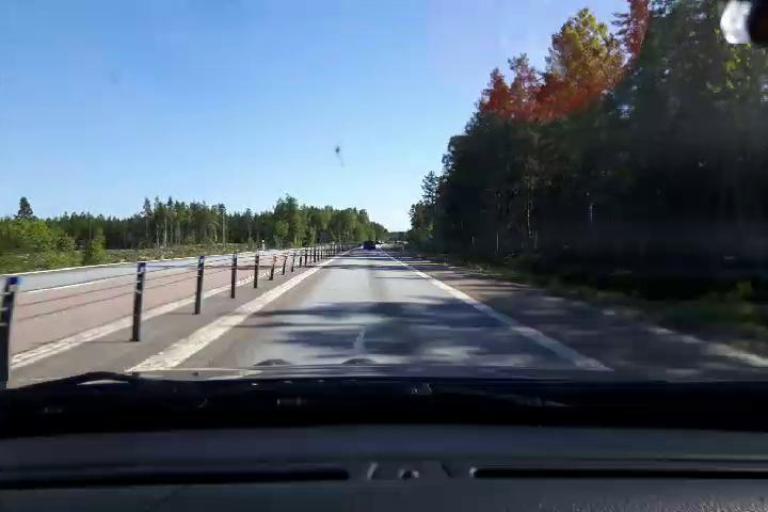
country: SE
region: Gaevleborg
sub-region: Gavle Kommun
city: Norrsundet
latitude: 60.8458
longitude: 17.0746
